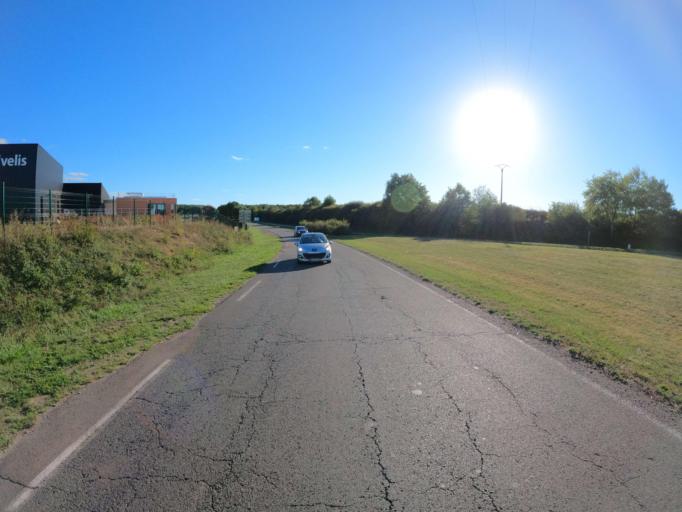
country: FR
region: Bourgogne
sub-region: Departement de Saone-et-Loire
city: Torcy
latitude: 46.7656
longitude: 4.4450
